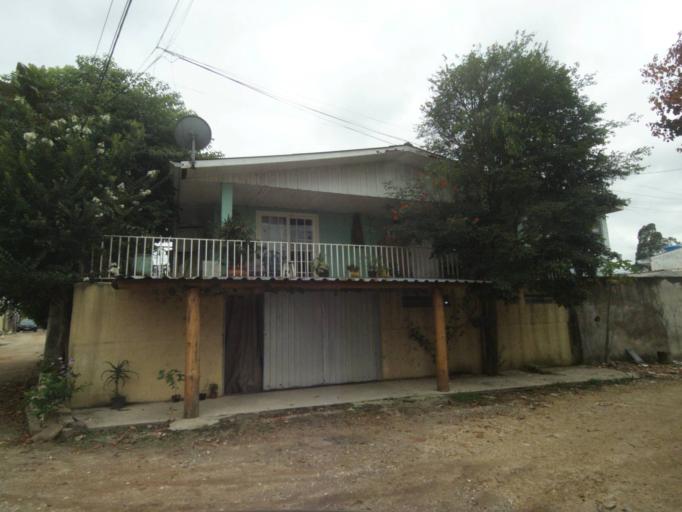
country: BR
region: Parana
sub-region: Pinhais
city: Pinhais
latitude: -25.4562
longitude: -49.1958
